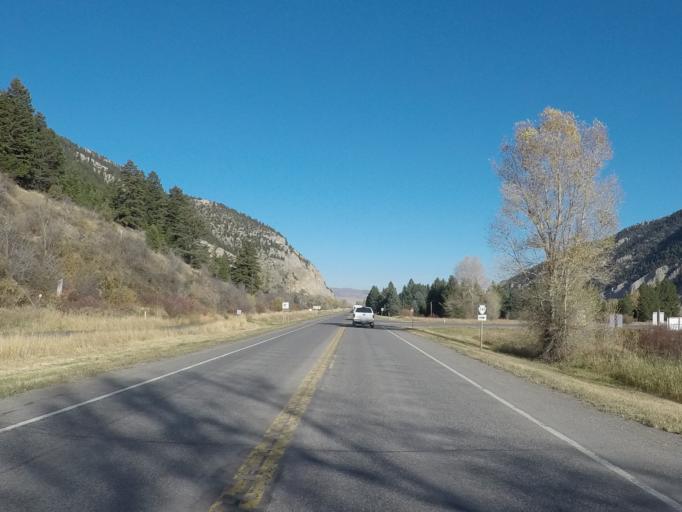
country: US
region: Montana
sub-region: Park County
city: Livingston
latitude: 45.5976
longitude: -110.5719
